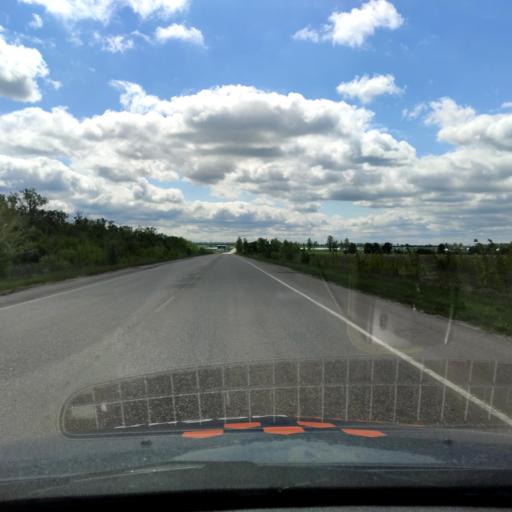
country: RU
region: Voronezj
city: Novaya Usman'
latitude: 51.6121
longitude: 39.3370
